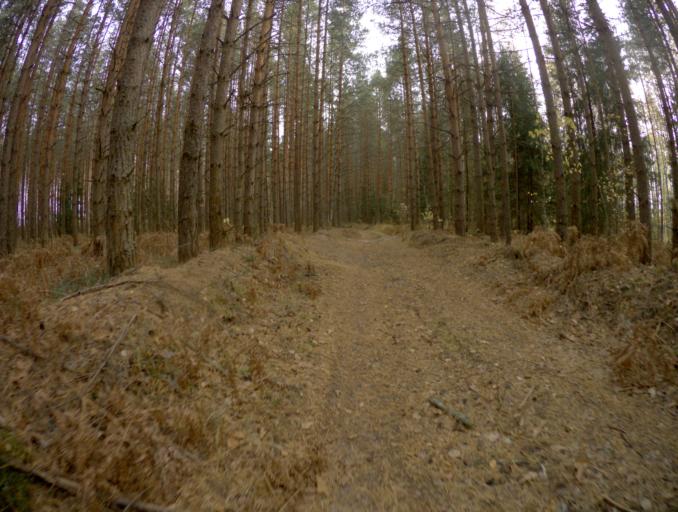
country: RU
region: Vladimir
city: Sobinka
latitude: 55.9721
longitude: 40.0766
